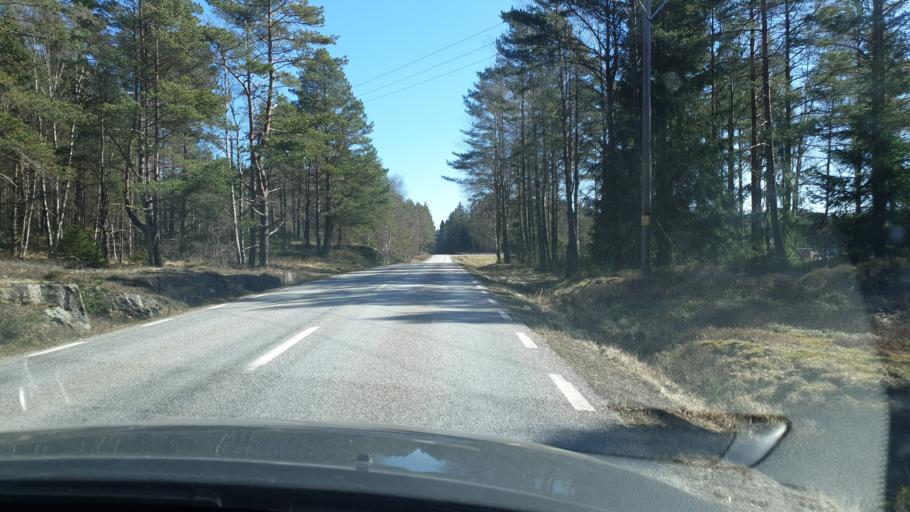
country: SE
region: Vaestra Goetaland
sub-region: Tanums Kommun
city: Tanumshede
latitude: 58.7422
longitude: 11.4641
